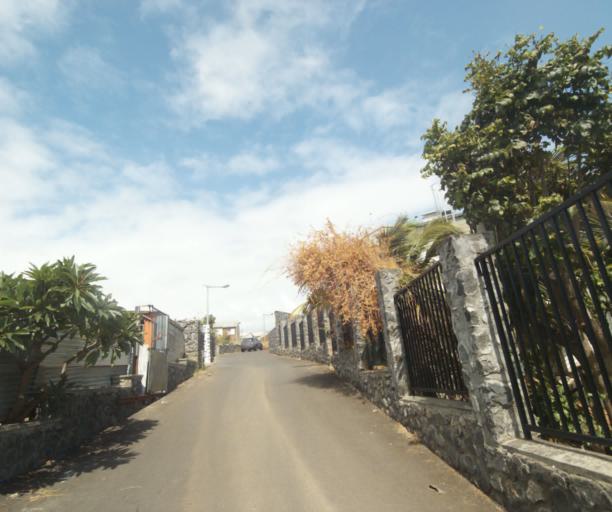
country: RE
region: Reunion
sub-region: Reunion
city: Saint-Paul
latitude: -21.0476
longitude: 55.2623
